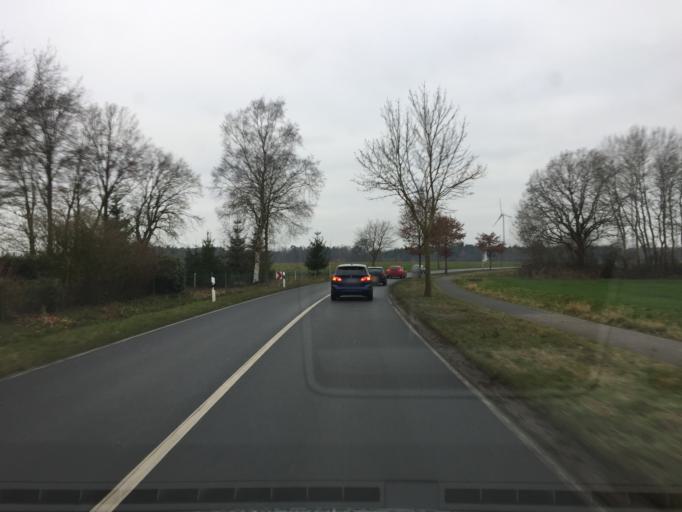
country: DE
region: Lower Saxony
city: Langwedel
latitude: 53.0051
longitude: 9.1748
